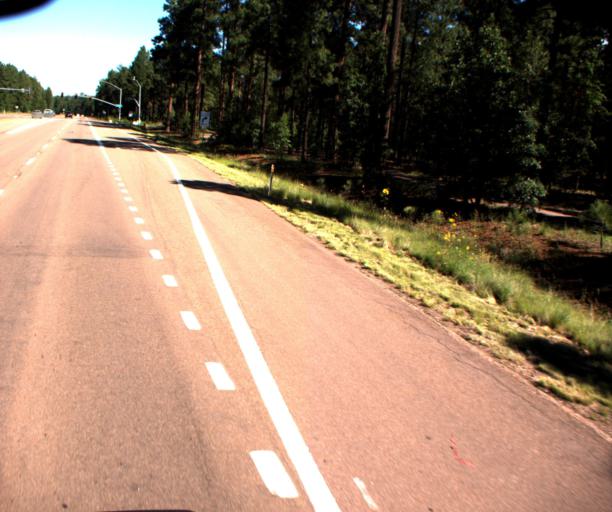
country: US
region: Arizona
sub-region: Navajo County
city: Pinetop-Lakeside
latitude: 34.1141
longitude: -109.9147
